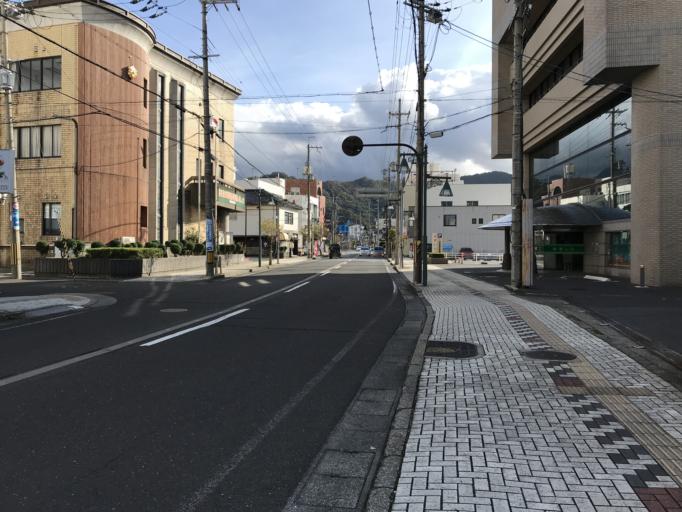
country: JP
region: Fukui
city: Obama
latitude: 35.4973
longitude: 135.7456
